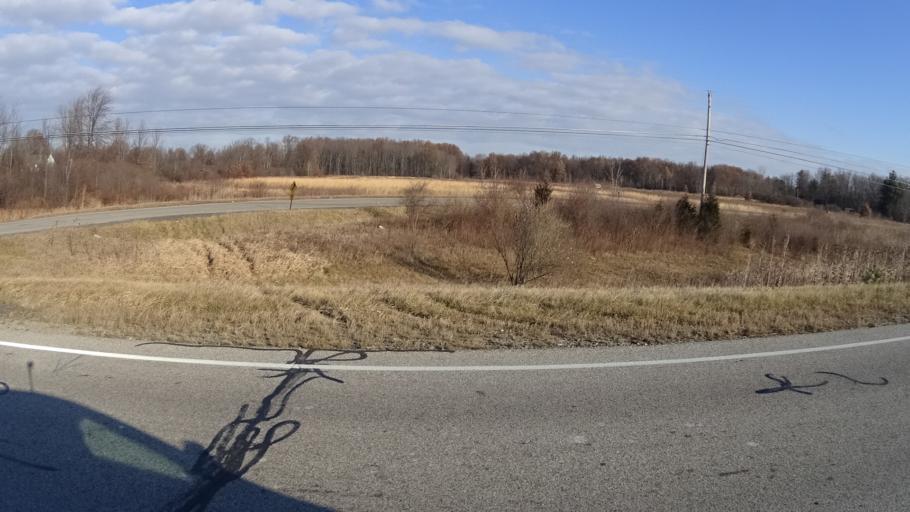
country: US
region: Ohio
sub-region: Lorain County
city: Oberlin
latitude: 41.2819
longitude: -82.1870
